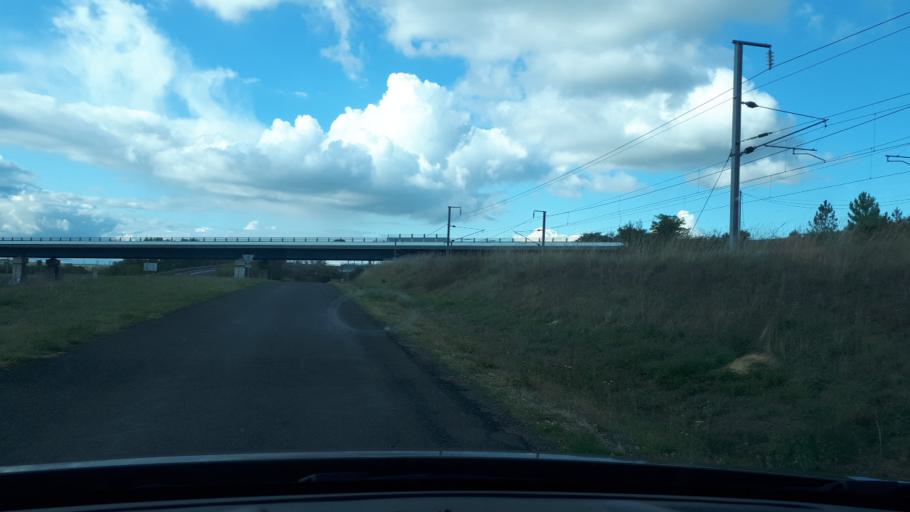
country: FR
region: Centre
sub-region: Departement du Loir-et-Cher
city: Mareuil-sur-Cher
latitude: 47.3030
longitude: 1.3505
